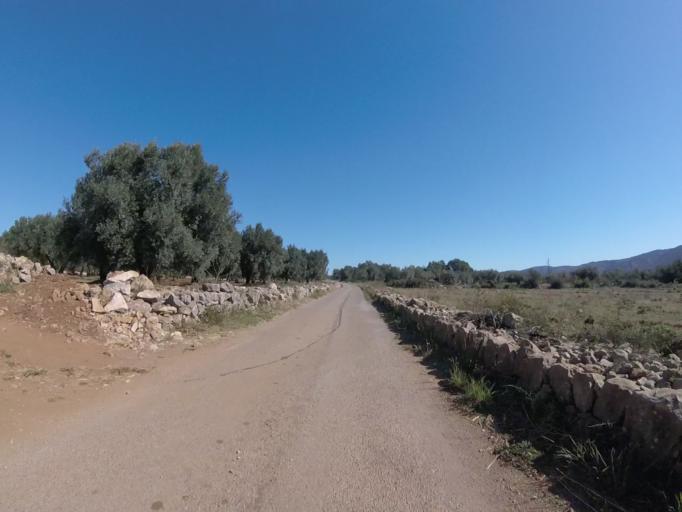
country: ES
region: Valencia
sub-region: Provincia de Castello
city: Santa Magdalena de Pulpis
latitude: 40.3545
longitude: 0.2828
